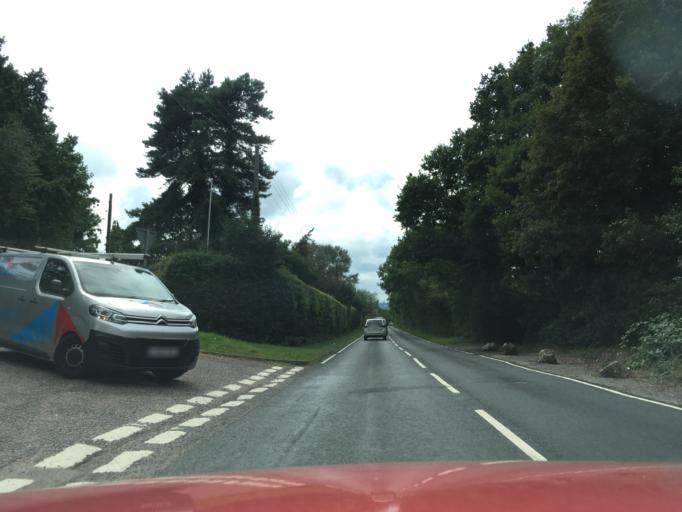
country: GB
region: England
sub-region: Kent
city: Marden
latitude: 51.1102
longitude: 0.4497
